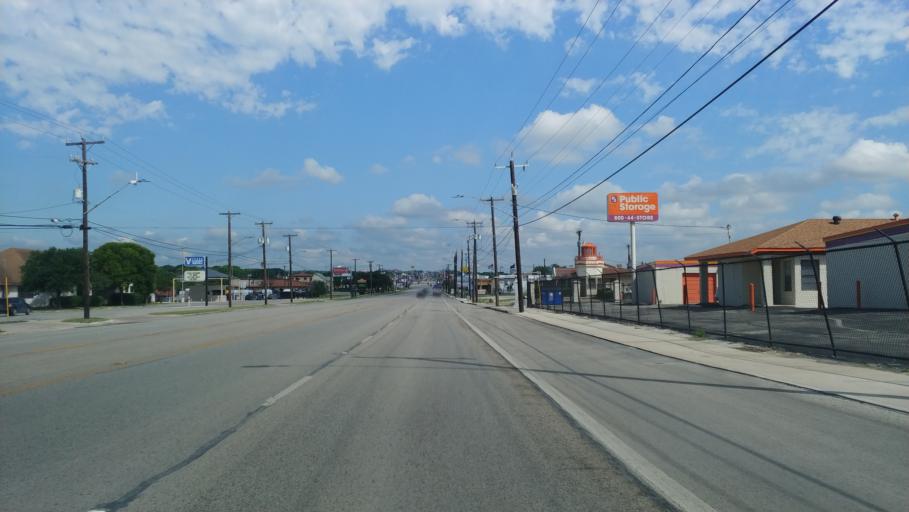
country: US
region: Texas
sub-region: Bexar County
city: Balcones Heights
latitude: 29.4752
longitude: -98.5366
